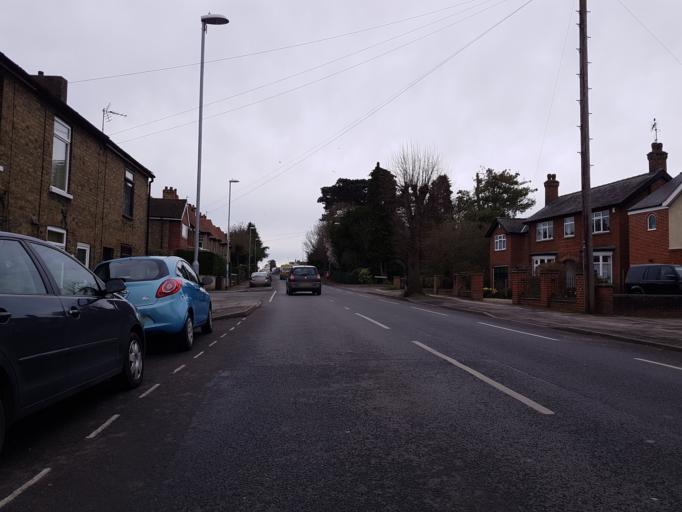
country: GB
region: England
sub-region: Cambridgeshire
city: Ely
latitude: 52.3970
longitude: 0.2555
